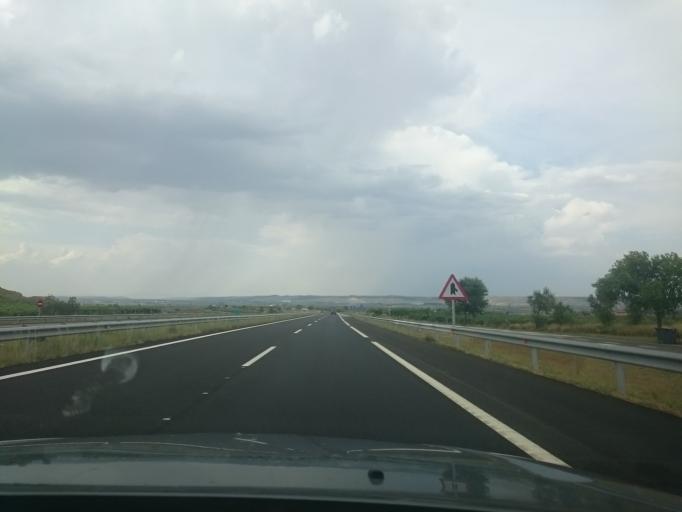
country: ES
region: La Rioja
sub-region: Provincia de La Rioja
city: Aldeanueva de Ebro
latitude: 42.2380
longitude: -1.9011
